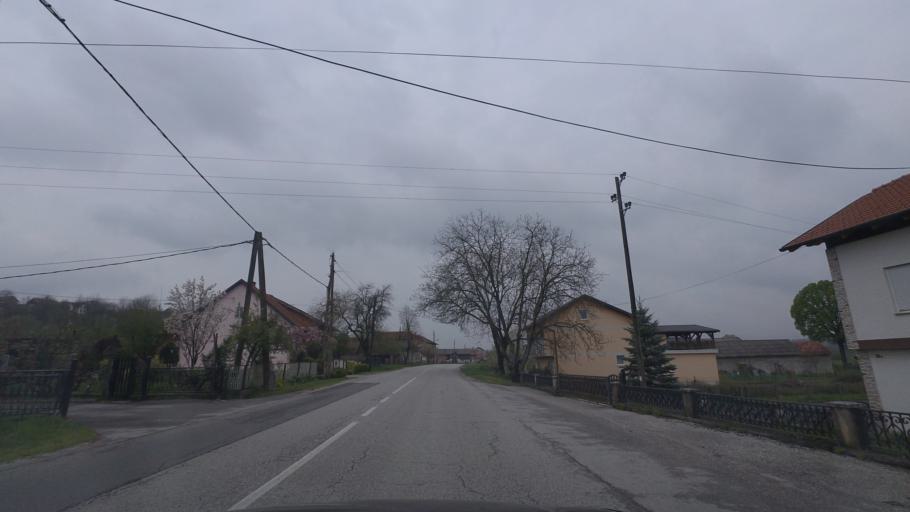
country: HR
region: Zagrebacka
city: Jastrebarsko
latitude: 45.6155
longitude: 15.5813
